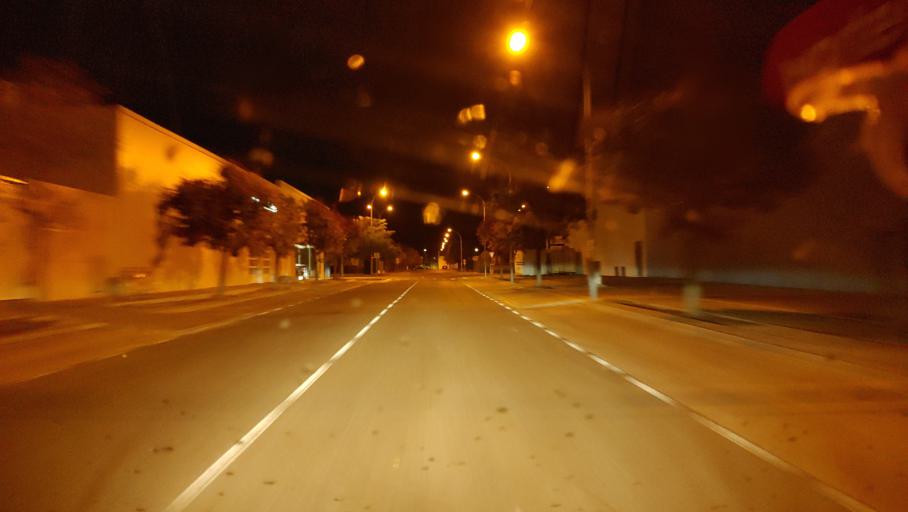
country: ES
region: Castille-La Mancha
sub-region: Provincia de Ciudad Real
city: Ciudad Real
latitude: 38.9849
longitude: -3.9086
